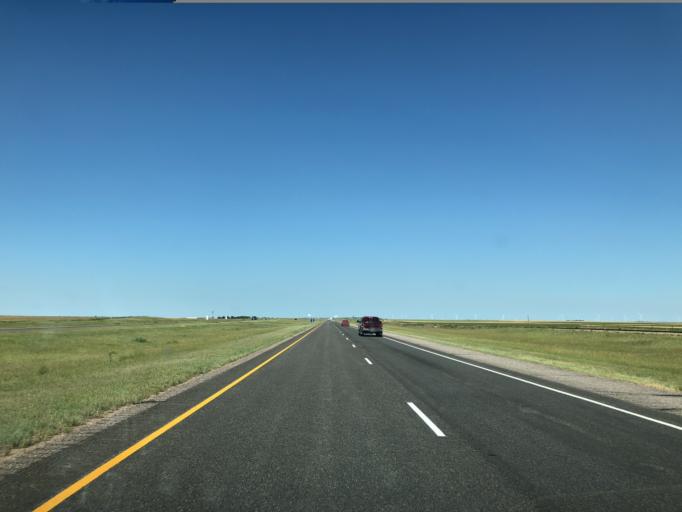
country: US
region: Colorado
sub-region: Lincoln County
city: Hugo
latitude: 39.2862
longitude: -103.1854
